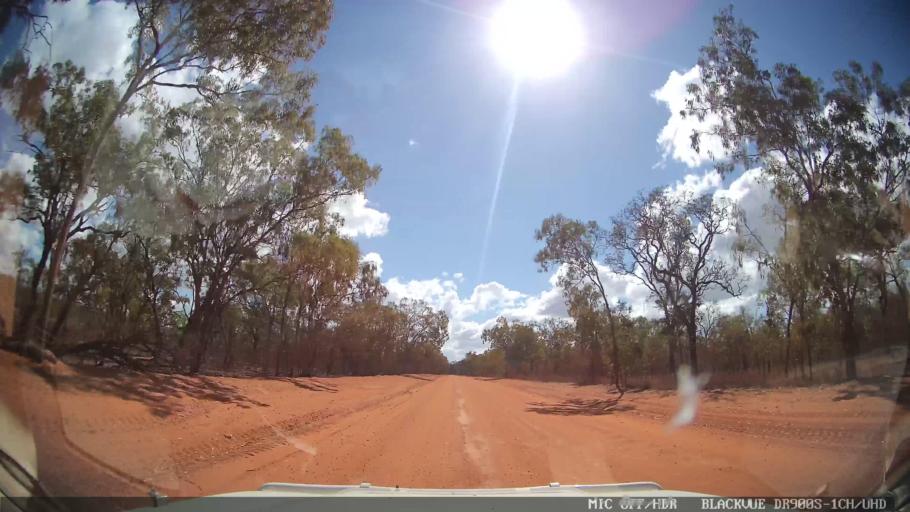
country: AU
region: Queensland
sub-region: Cook
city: Cooktown
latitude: -15.1941
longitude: 144.3773
